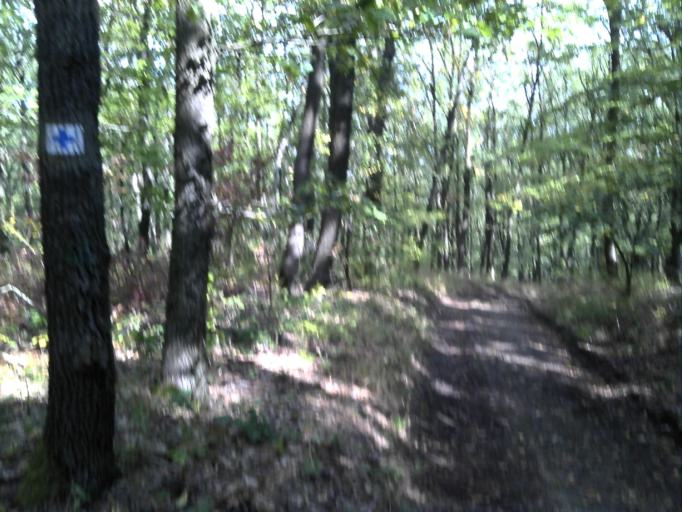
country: HU
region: Borsod-Abauj-Zemplen
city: Satoraljaujhely
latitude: 48.3923
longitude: 21.6241
